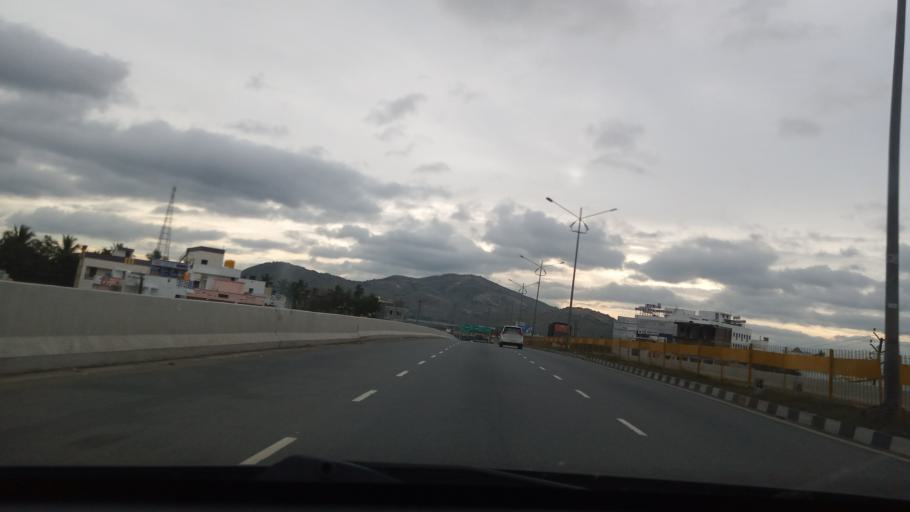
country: IN
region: Tamil Nadu
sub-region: Krishnagiri
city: Krishnagiri
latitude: 12.5100
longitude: 78.2257
